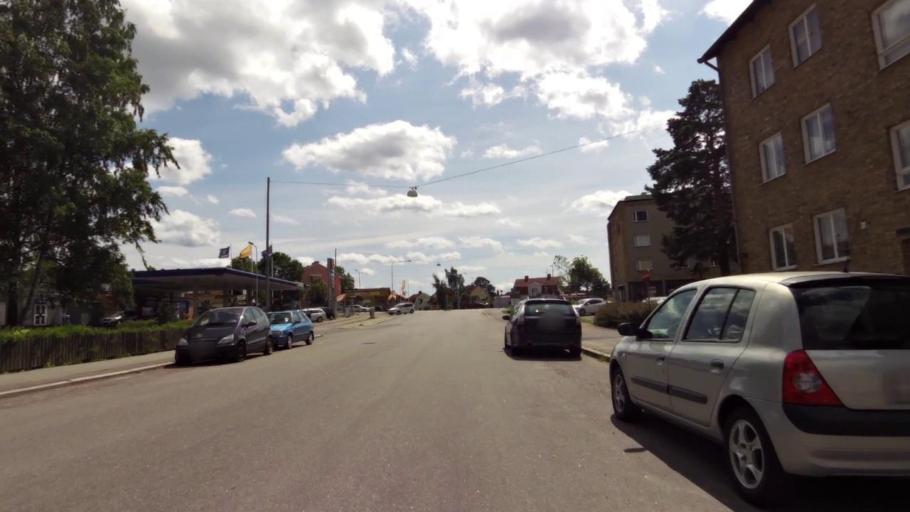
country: SE
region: OEstergoetland
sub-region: Linkopings Kommun
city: Linkoping
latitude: 58.4084
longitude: 15.5968
